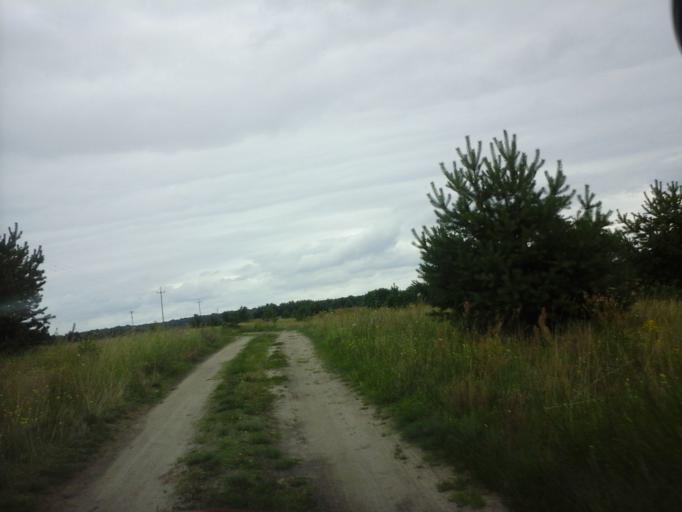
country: PL
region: Lubusz
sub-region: Powiat strzelecko-drezdenecki
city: Dobiegniew
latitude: 53.0822
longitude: 15.7811
